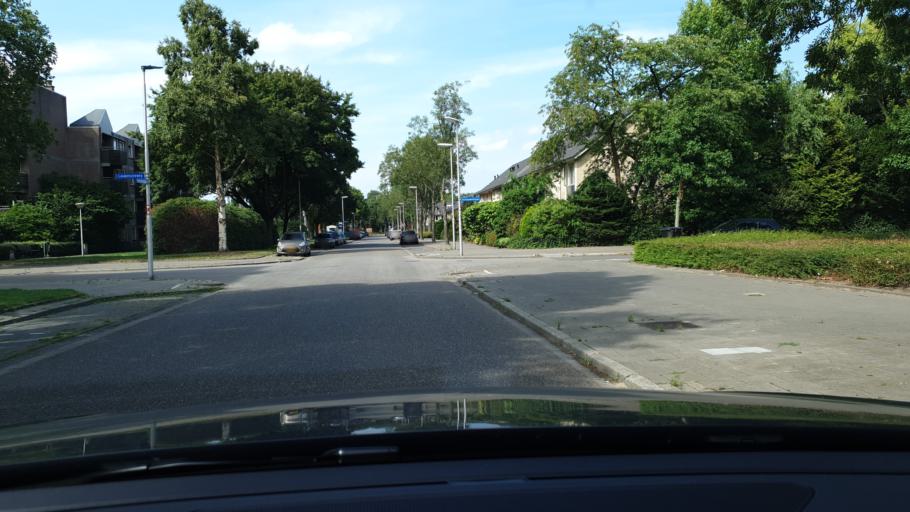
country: NL
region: North Brabant
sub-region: Gemeente Eindhoven
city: Eindhoven
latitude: 51.4788
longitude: 5.4664
